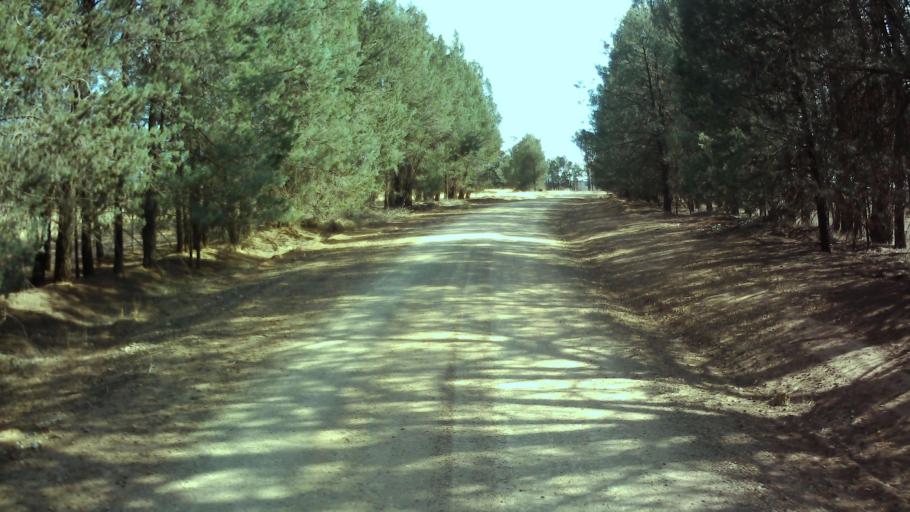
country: AU
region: New South Wales
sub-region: Weddin
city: Grenfell
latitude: -33.7698
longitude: 148.0469
